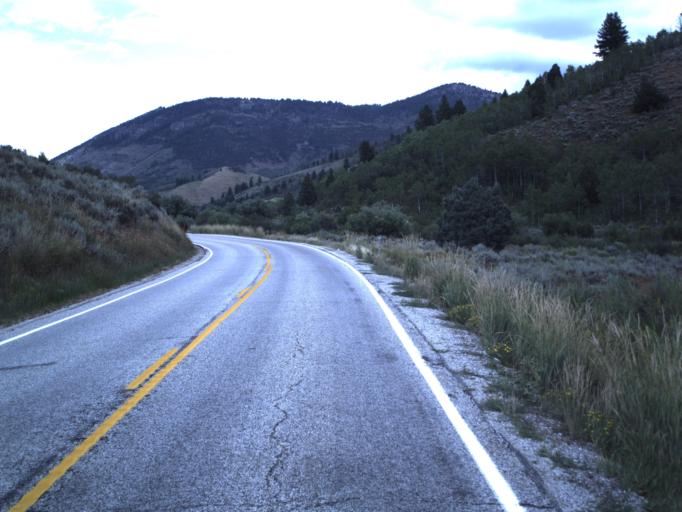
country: US
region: Utah
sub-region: Cache County
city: Richmond
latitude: 41.8621
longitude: -111.5724
